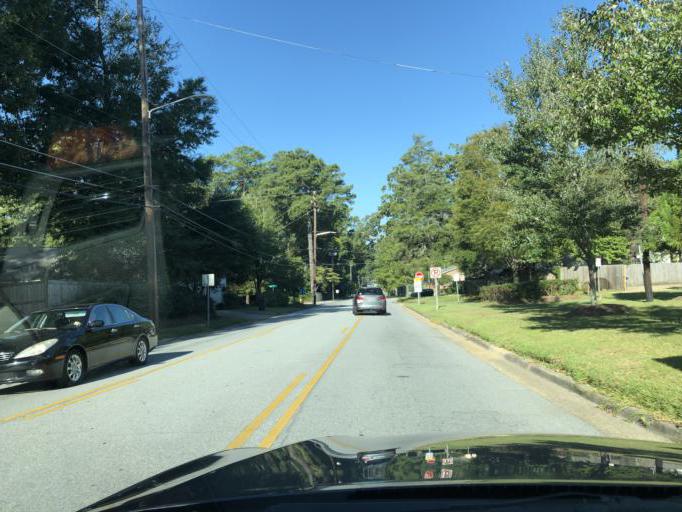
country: US
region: Georgia
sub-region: Muscogee County
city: Columbus
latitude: 32.4786
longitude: -84.9602
